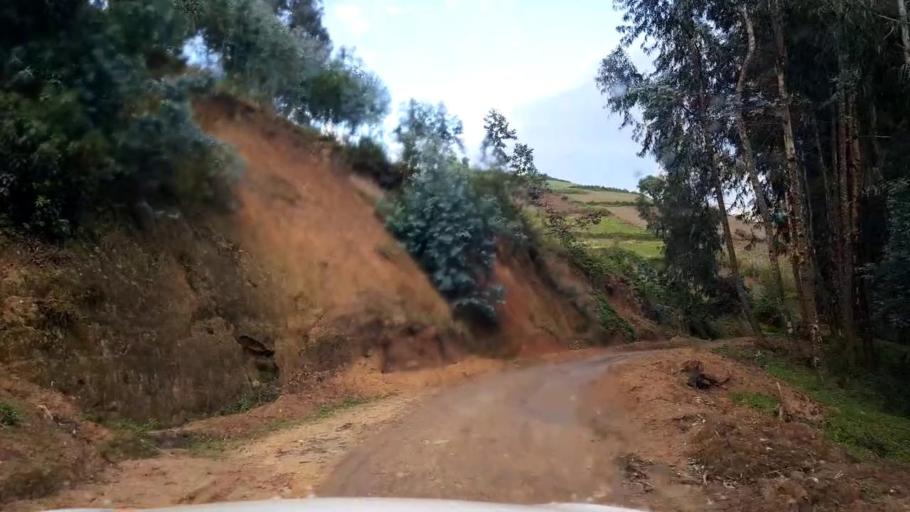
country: RW
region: Southern Province
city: Gitarama
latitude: -1.8647
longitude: 29.5700
